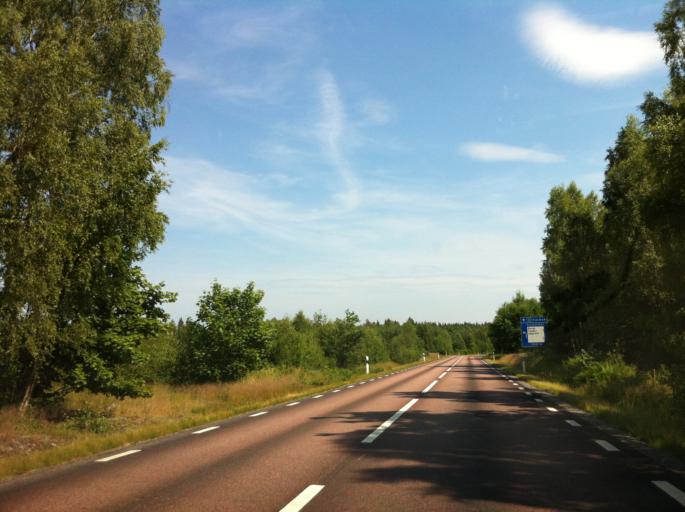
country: SE
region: Kalmar
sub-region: Nybro Kommun
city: Nybro
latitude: 56.8207
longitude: 15.7703
